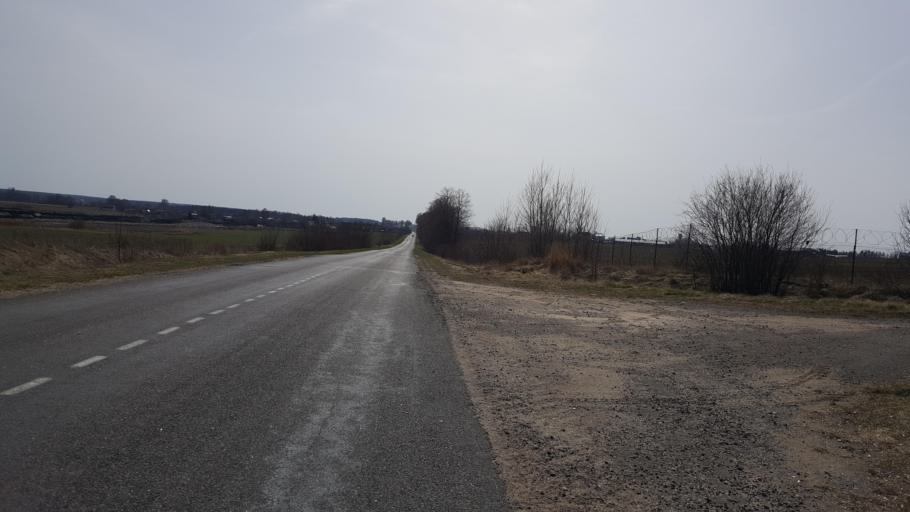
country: BY
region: Brest
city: Kamyanyets
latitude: 52.4147
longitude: 23.8021
